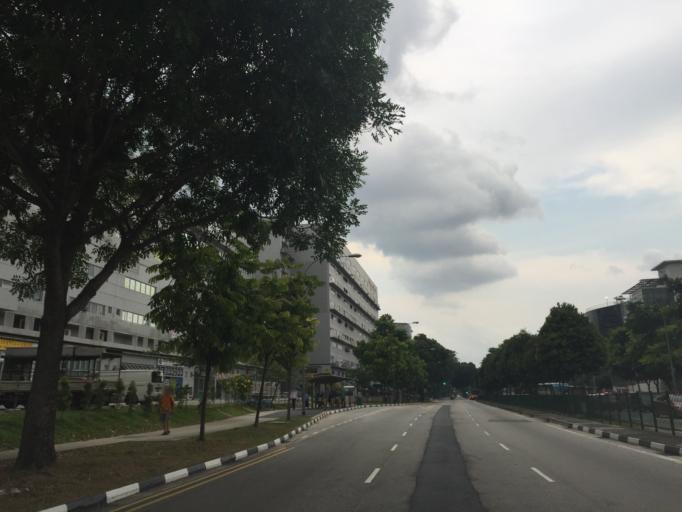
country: MY
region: Johor
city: Johor Bahru
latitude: 1.3342
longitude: 103.6966
